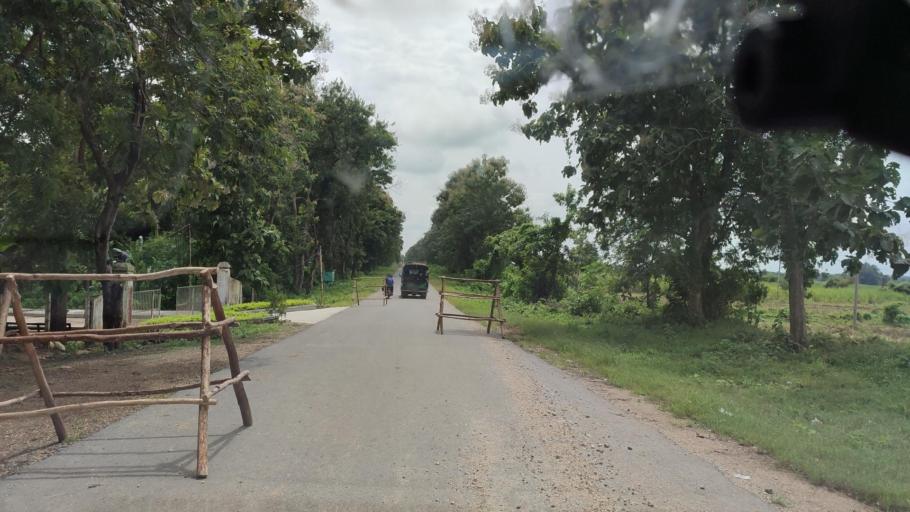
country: MM
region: Bago
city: Pyay
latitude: 18.8713
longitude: 95.2382
